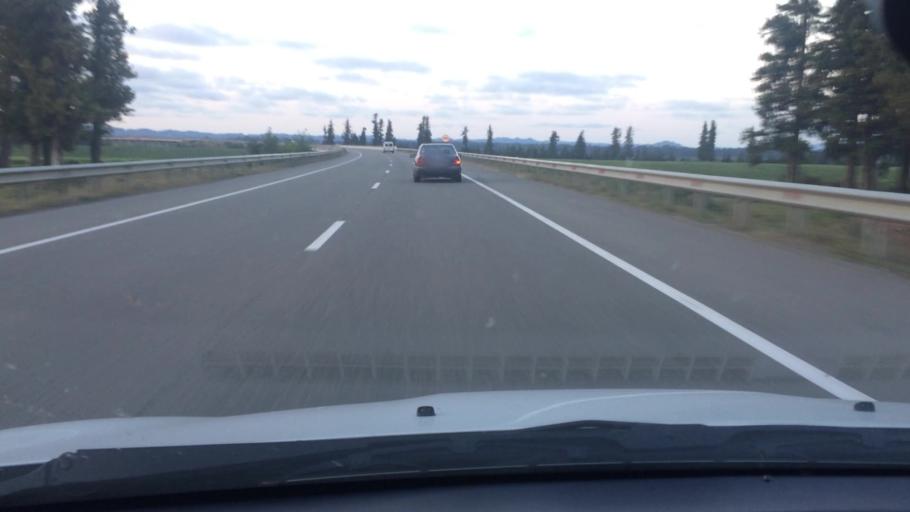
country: GE
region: Ajaria
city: Ochkhamuri
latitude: 41.8571
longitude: 41.8383
